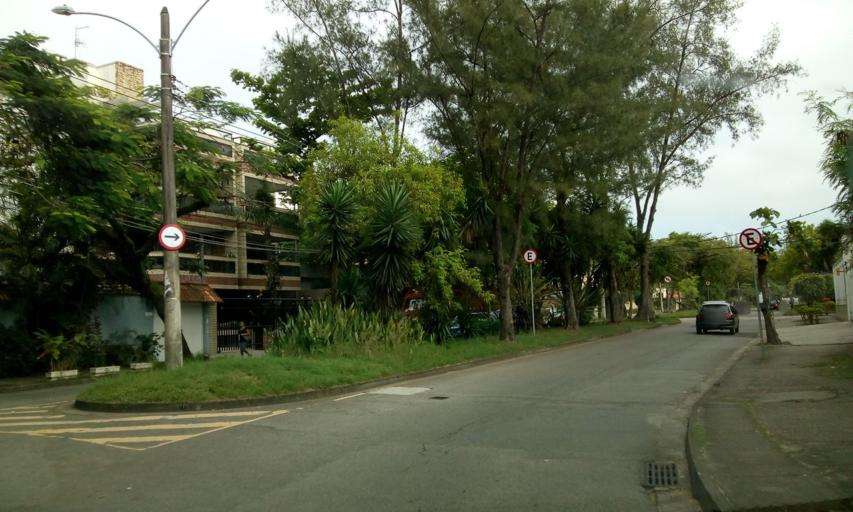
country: BR
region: Rio de Janeiro
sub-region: Nilopolis
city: Nilopolis
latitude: -23.0153
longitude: -43.4550
